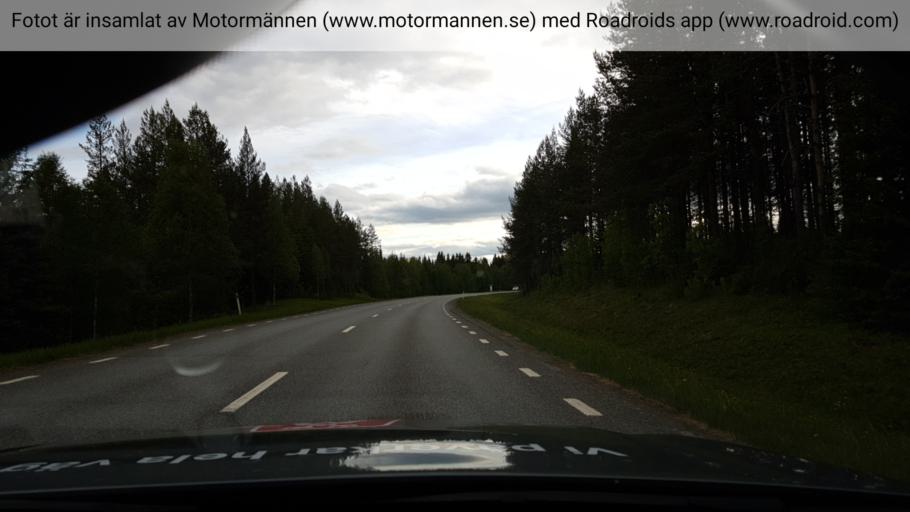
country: SE
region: Jaemtland
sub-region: OEstersunds Kommun
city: Lit
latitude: 63.4863
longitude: 15.2385
